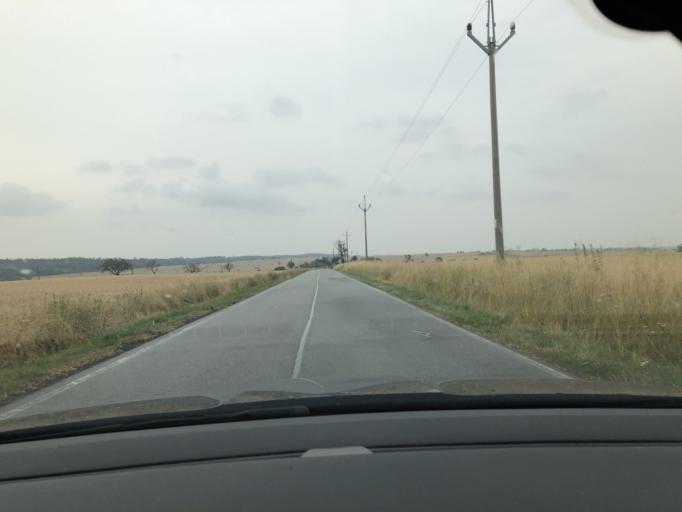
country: CZ
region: South Moravian
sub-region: Okres Znojmo
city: Jevisovice
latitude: 49.0291
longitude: 16.0246
